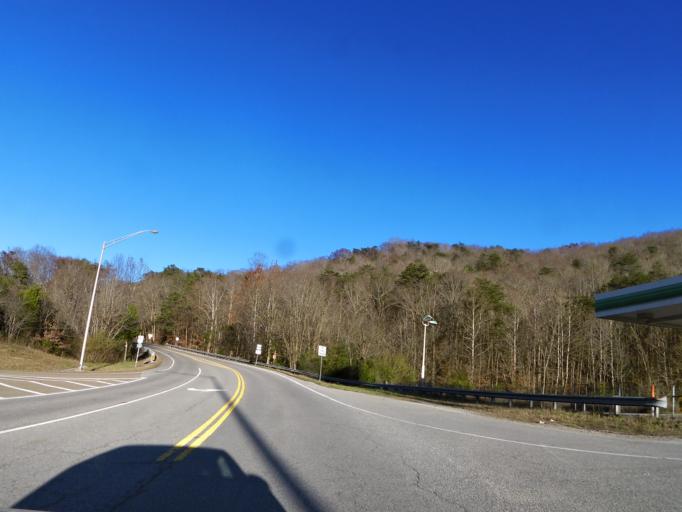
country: US
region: Tennessee
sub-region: Anderson County
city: Rocky Top
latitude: 36.2273
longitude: -84.1502
